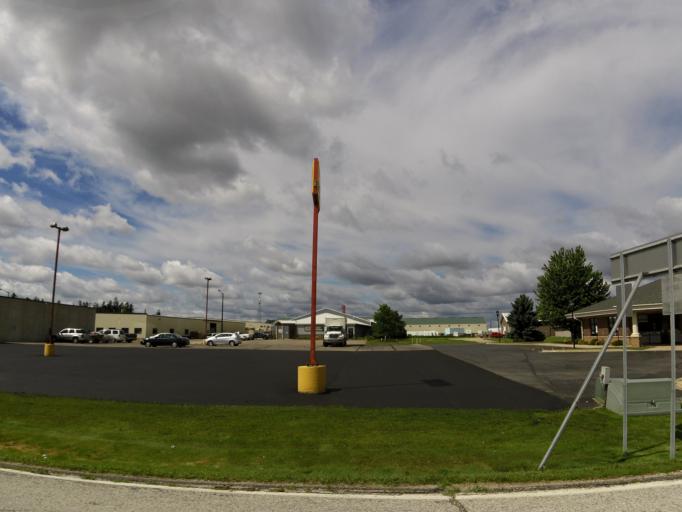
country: US
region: Minnesota
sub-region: Fillmore County
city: Spring Valley
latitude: 43.7013
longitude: -92.4018
